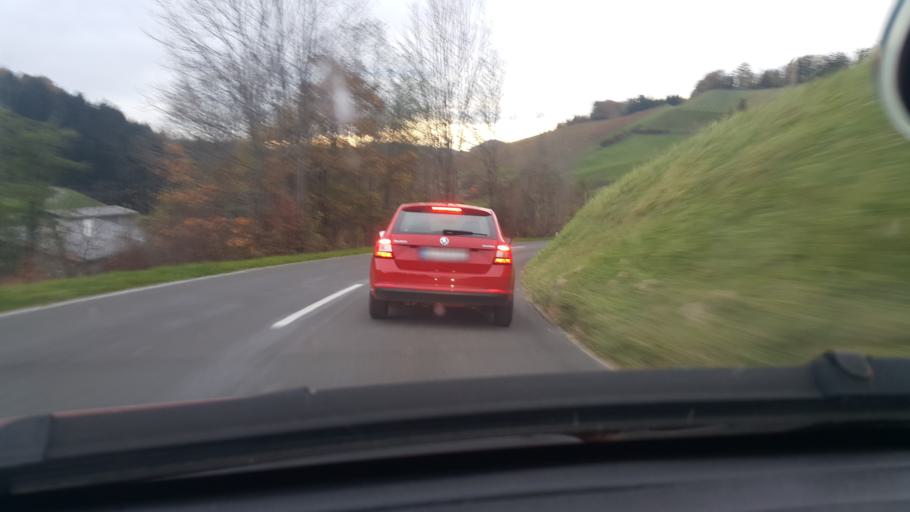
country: AT
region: Styria
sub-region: Politischer Bezirk Leibnitz
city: Leutschach
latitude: 46.6442
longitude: 15.5083
